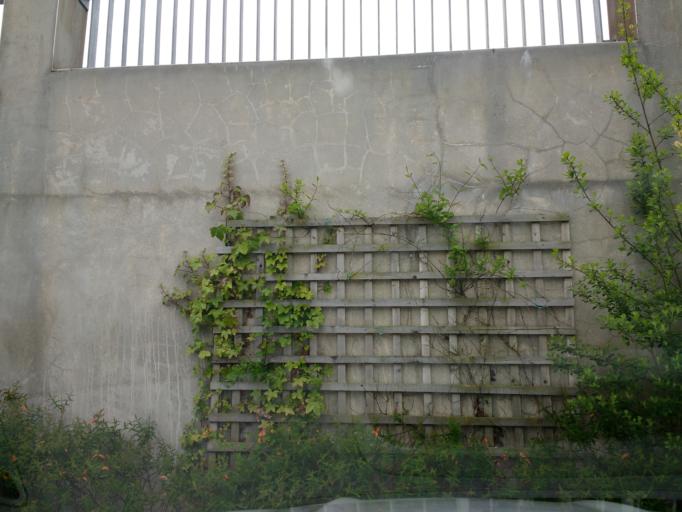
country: IE
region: Ulster
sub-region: County Donegal
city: Ramelton
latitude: 55.0819
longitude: -7.6867
